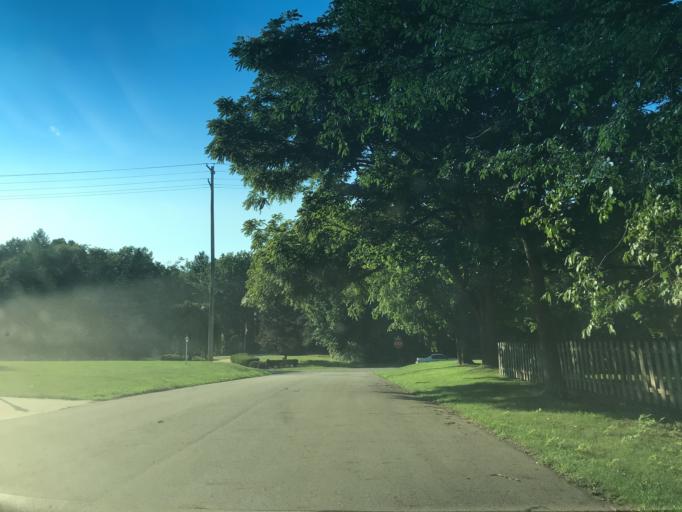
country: US
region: Michigan
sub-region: Eaton County
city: Waverly
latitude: 42.7068
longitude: -84.6112
